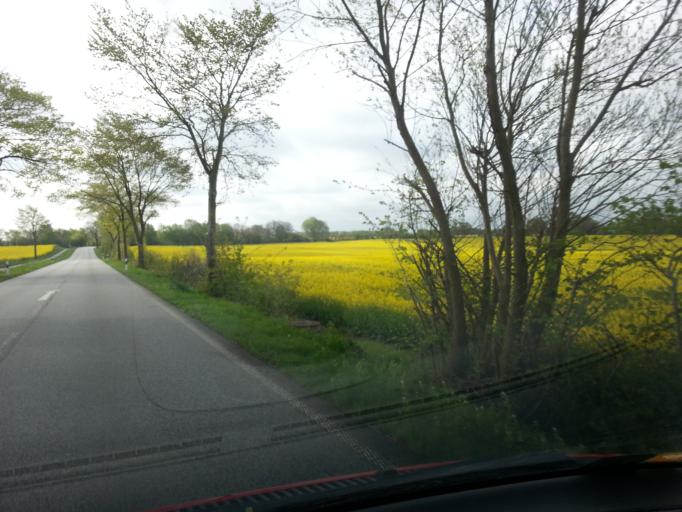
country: DE
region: Schleswig-Holstein
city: Travemuende
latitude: 53.9815
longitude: 10.8460
